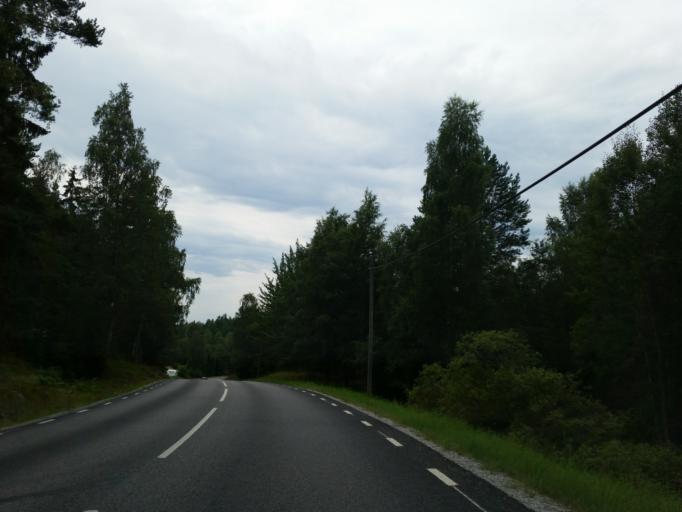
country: SE
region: Stockholm
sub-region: Sodertalje Kommun
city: Soedertaelje
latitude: 59.2192
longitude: 17.6673
